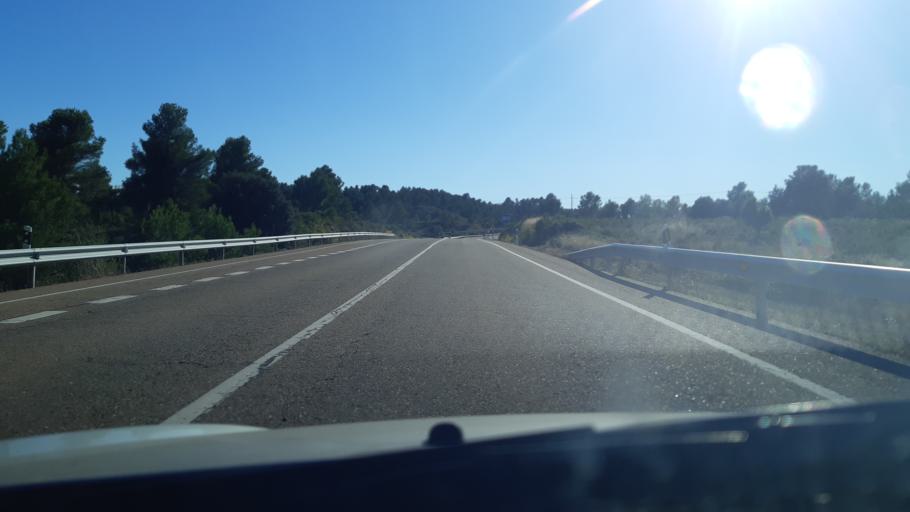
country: ES
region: Aragon
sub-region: Provincia de Teruel
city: Fornoles
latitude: 40.9167
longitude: -0.0194
